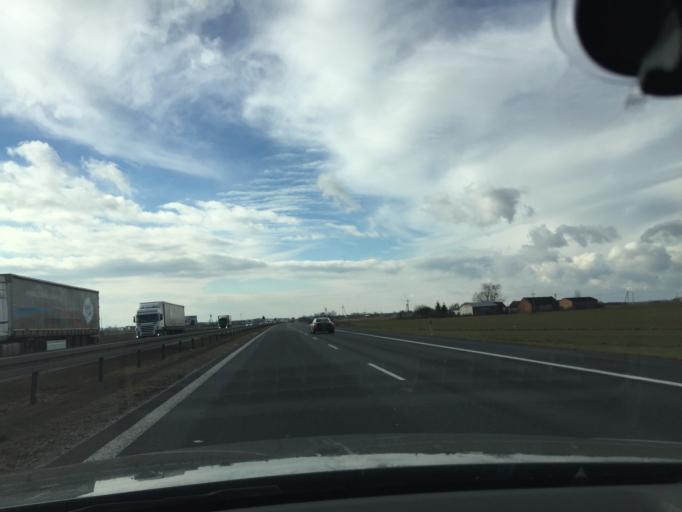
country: PL
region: Lodz Voivodeship
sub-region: Powiat piotrkowski
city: Wola Krzysztoporska
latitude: 51.3791
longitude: 19.6228
